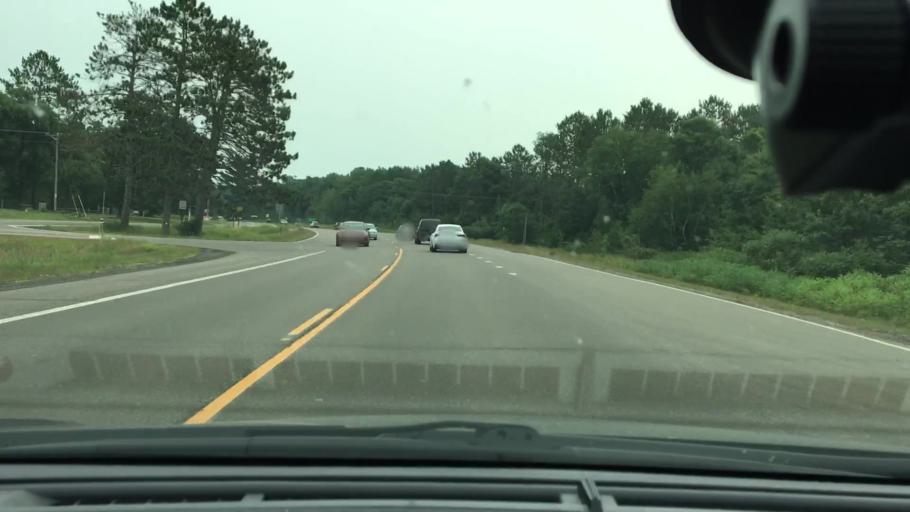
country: US
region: Minnesota
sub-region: Mille Lacs County
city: Vineland
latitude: 46.1131
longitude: -93.6569
